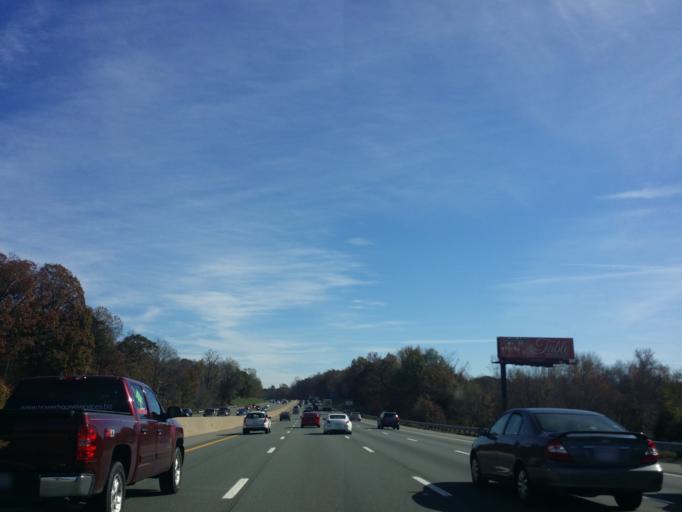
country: US
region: North Carolina
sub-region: Alamance County
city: Haw River
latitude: 36.0670
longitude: -79.3282
